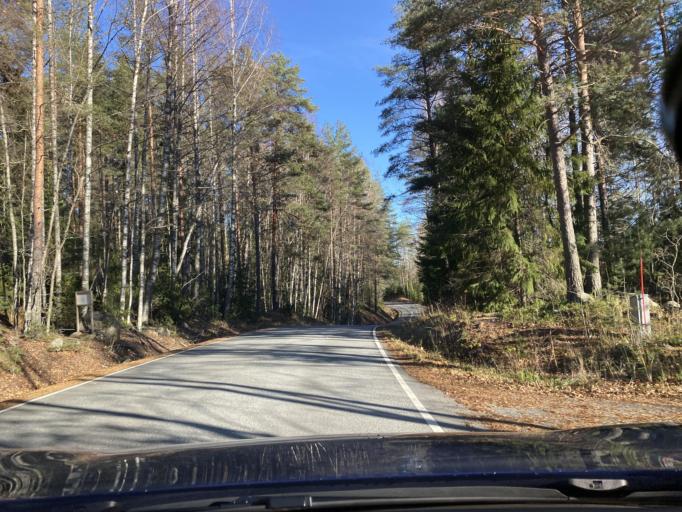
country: FI
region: Haeme
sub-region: Haemeenlinna
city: Kalvola
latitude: 61.0150
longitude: 24.1343
